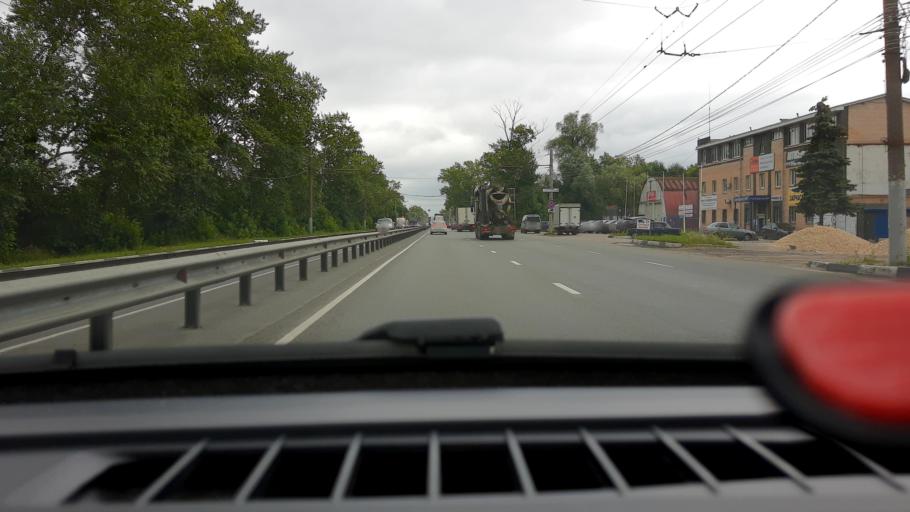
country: RU
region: Nizjnij Novgorod
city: Gorbatovka
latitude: 56.3111
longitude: 43.8222
